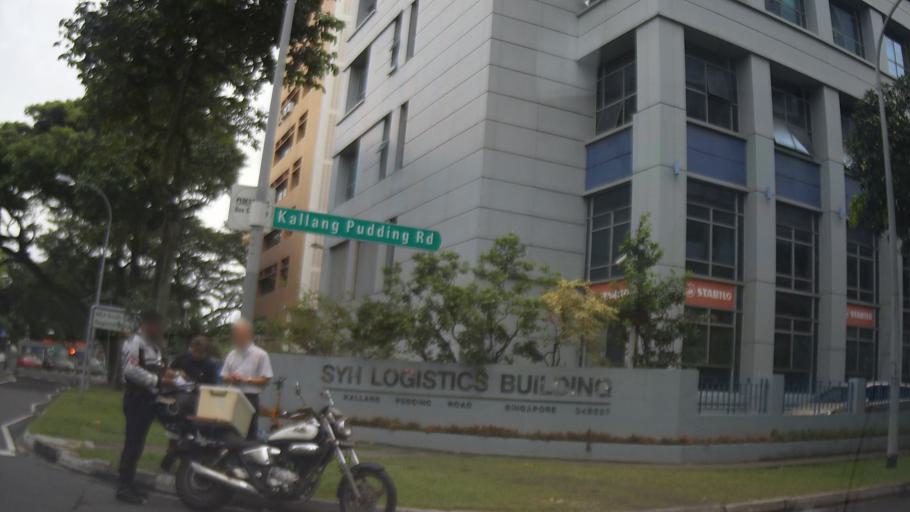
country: SG
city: Singapore
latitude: 1.3282
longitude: 103.8794
